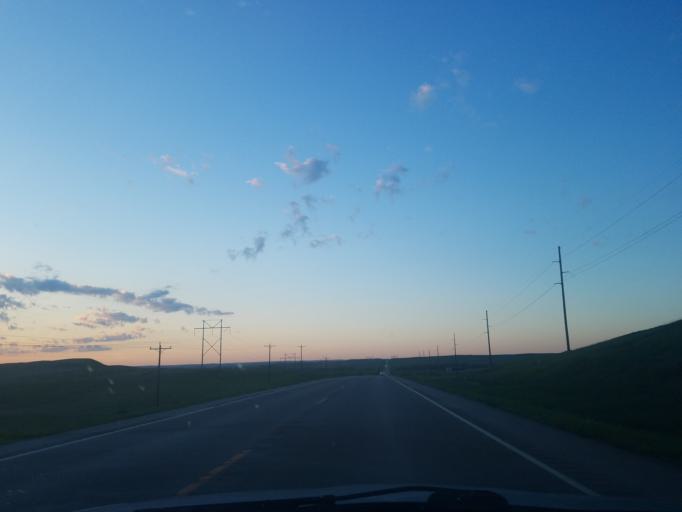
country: US
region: North Dakota
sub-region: McKenzie County
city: Watford City
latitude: 47.7051
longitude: -103.2835
